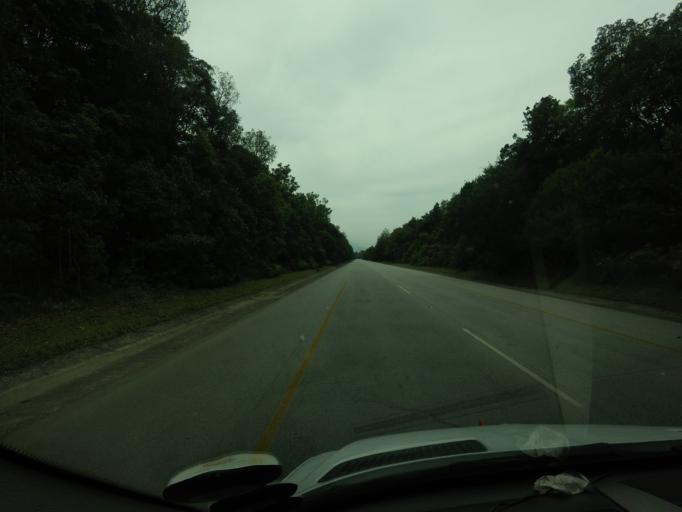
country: ZA
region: Eastern Cape
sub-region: Cacadu District Municipality
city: Kareedouw
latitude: -33.9700
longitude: 23.8497
